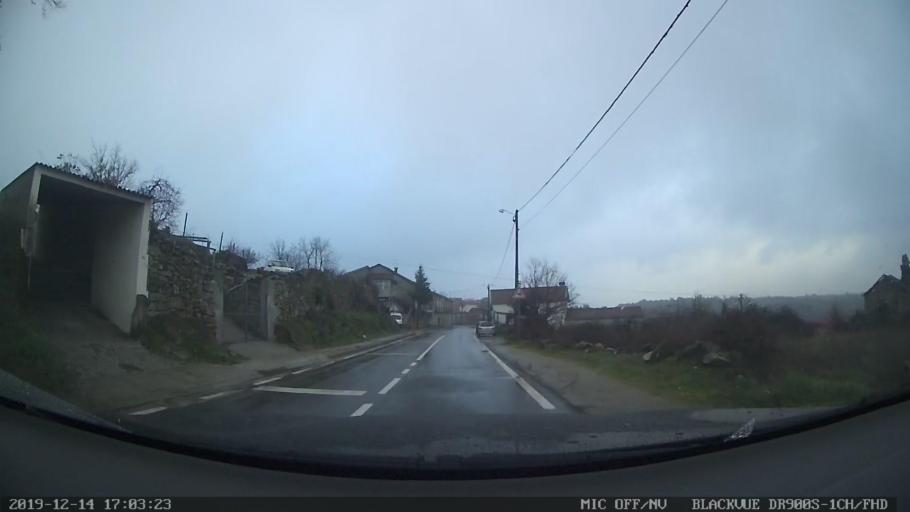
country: PT
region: Vila Real
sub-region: Vila Pouca de Aguiar
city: Vila Pouca de Aguiar
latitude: 41.4424
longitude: -7.5711
